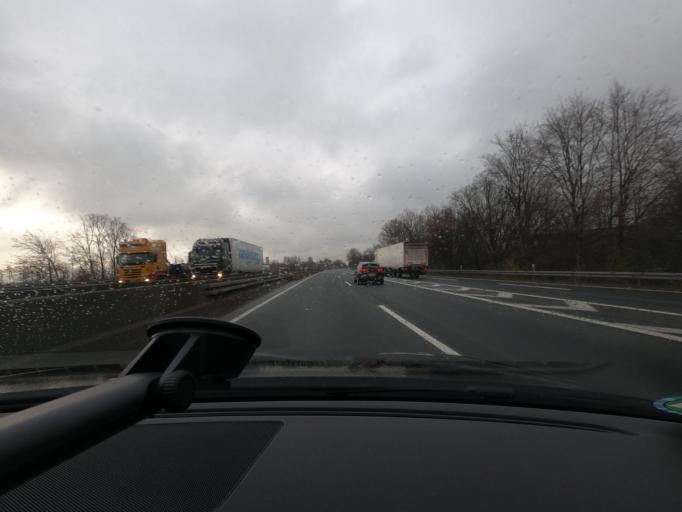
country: DE
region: North Rhine-Westphalia
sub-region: Regierungsbezirk Detmold
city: Wunnenberg
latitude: 51.5804
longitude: 8.7231
